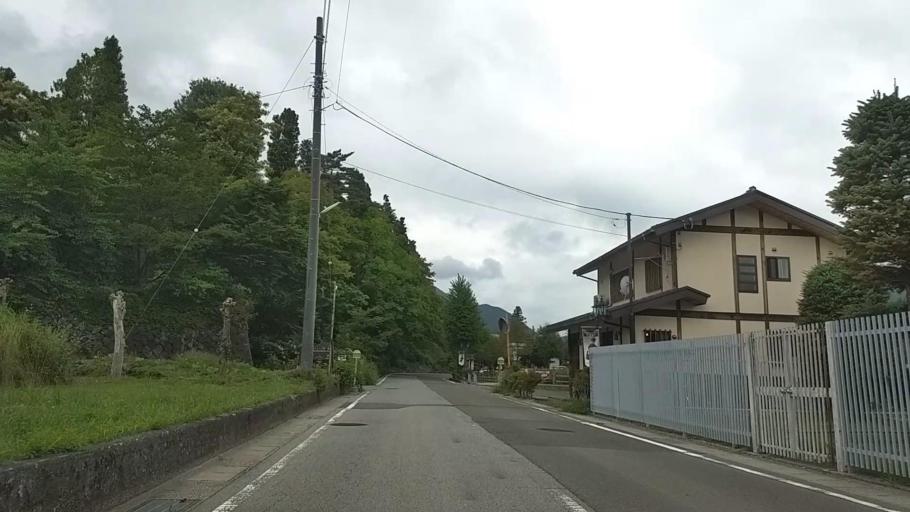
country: JP
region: Yamanashi
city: Fujikawaguchiko
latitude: 35.5105
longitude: 138.7523
